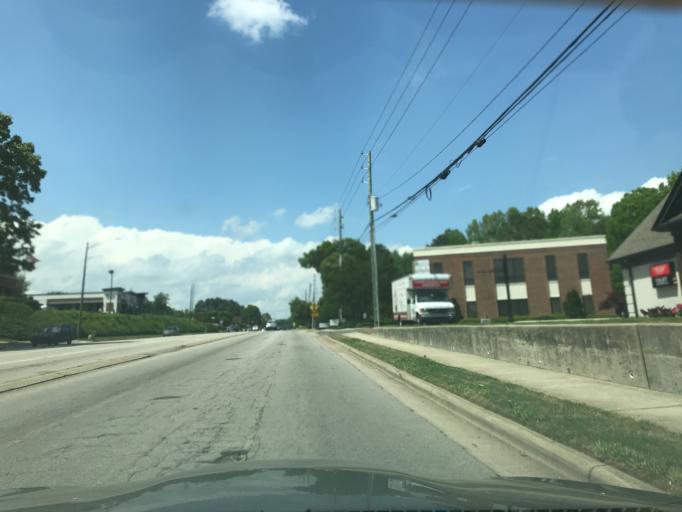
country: US
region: North Carolina
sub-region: Wake County
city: West Raleigh
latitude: 35.8791
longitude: -78.6457
